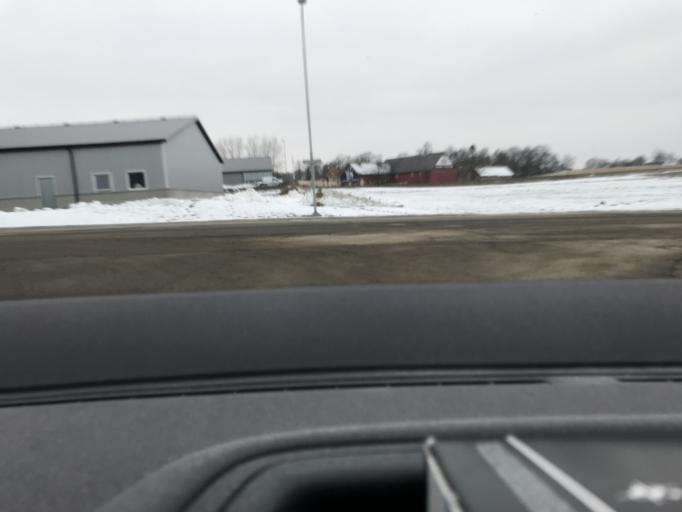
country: SE
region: Skane
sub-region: Ystads Kommun
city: Ystad
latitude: 55.4512
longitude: 13.8505
